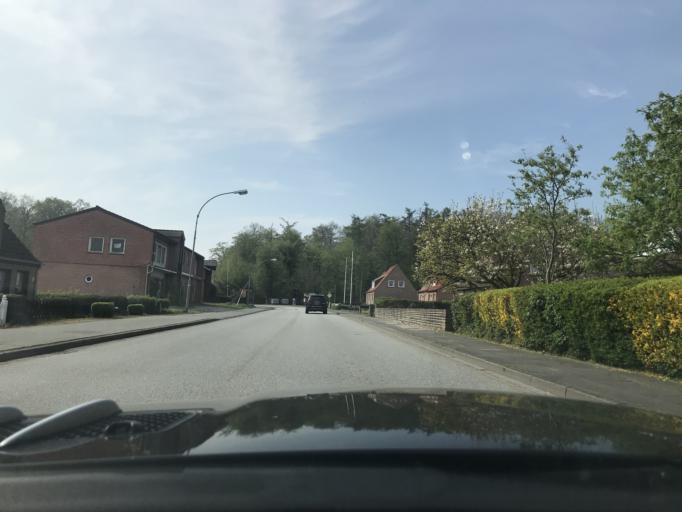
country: DE
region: Schleswig-Holstein
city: Riepsdorf
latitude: 54.1872
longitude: 10.9817
